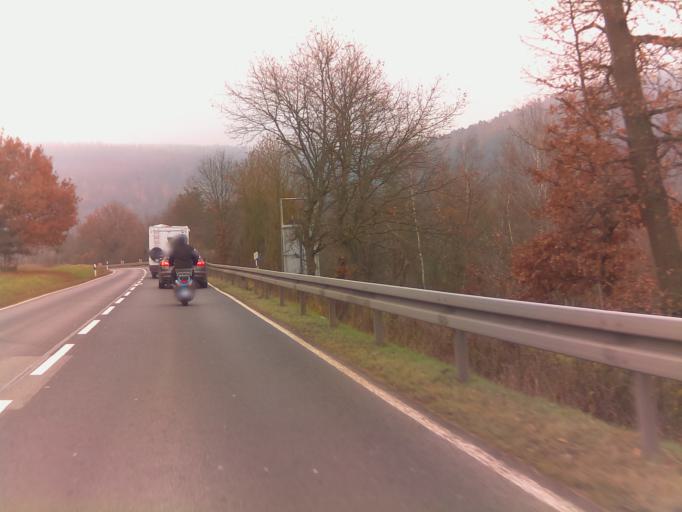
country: DE
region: Bavaria
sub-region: Regierungsbezirk Unterfranken
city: Faulbach
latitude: 49.7745
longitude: 9.4563
